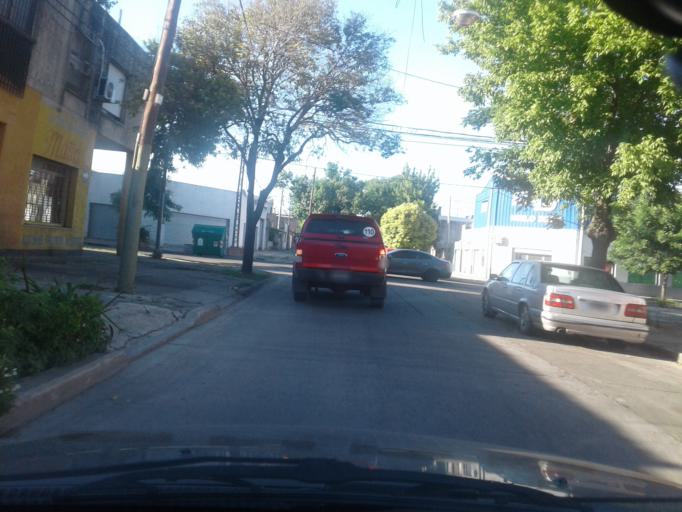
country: AR
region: Santa Fe
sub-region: Departamento de Rosario
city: Rosario
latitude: -32.9476
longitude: -60.6869
